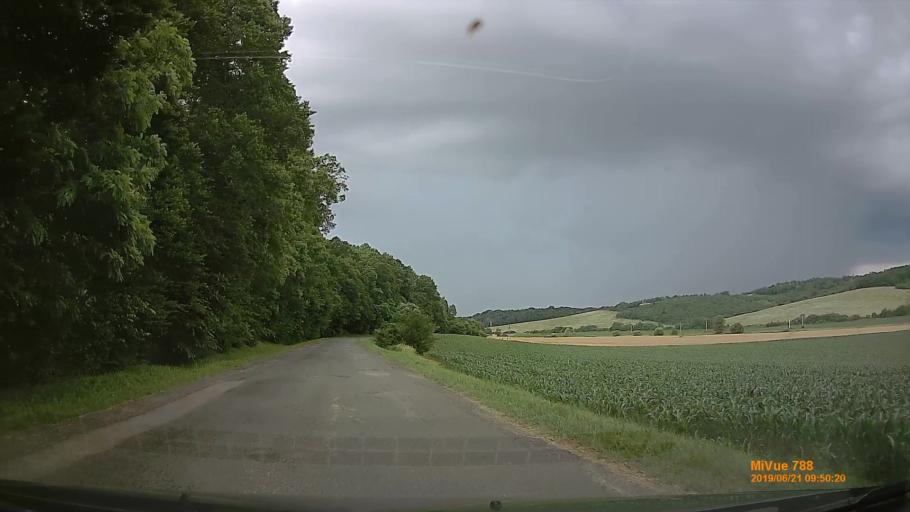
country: HU
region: Baranya
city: Sasd
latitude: 46.2606
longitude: 18.0329
